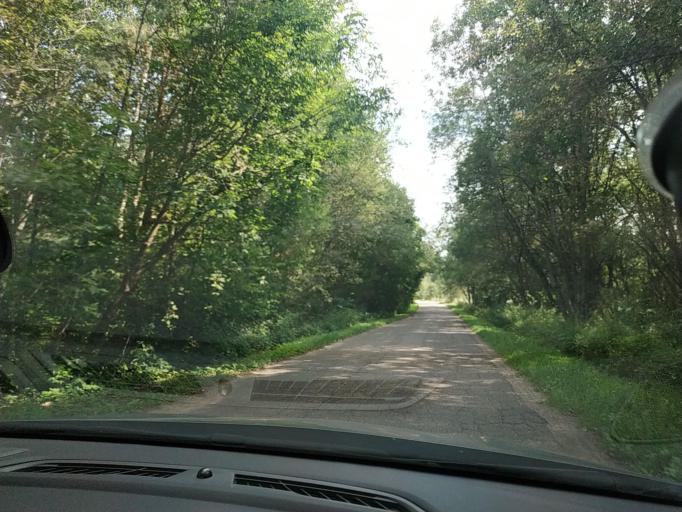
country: LT
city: Nemencine
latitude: 54.8485
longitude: 25.4537
